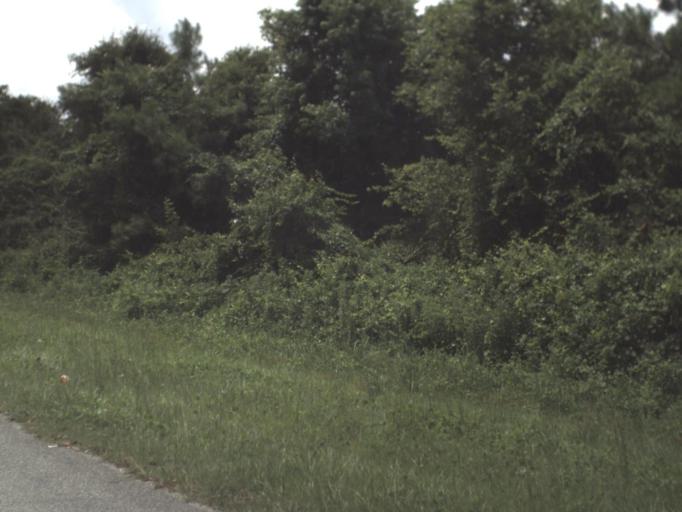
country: US
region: Florida
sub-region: Columbia County
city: Watertown
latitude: 30.1779
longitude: -82.5916
